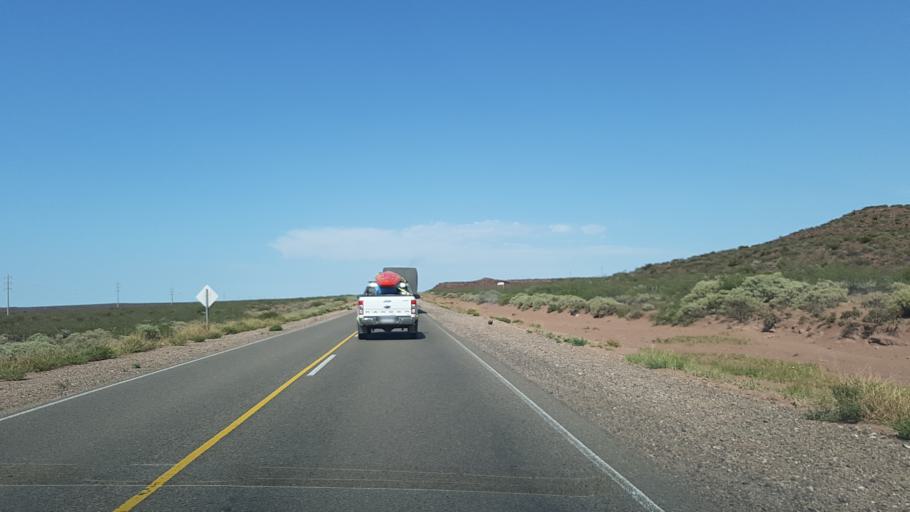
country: AR
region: Neuquen
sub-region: Departamento de Picun Leufu
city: Picun Leufu
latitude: -39.2856
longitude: -68.8682
